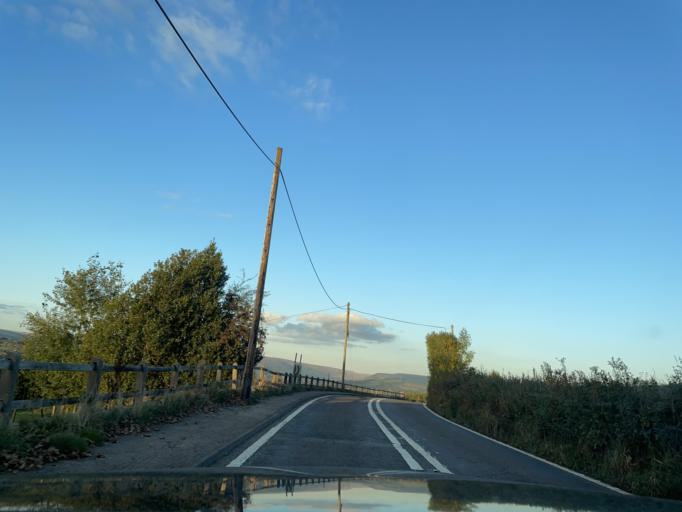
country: GB
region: England
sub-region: Borough of Tameside
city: Longdendale
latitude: 53.4256
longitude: -2.0251
